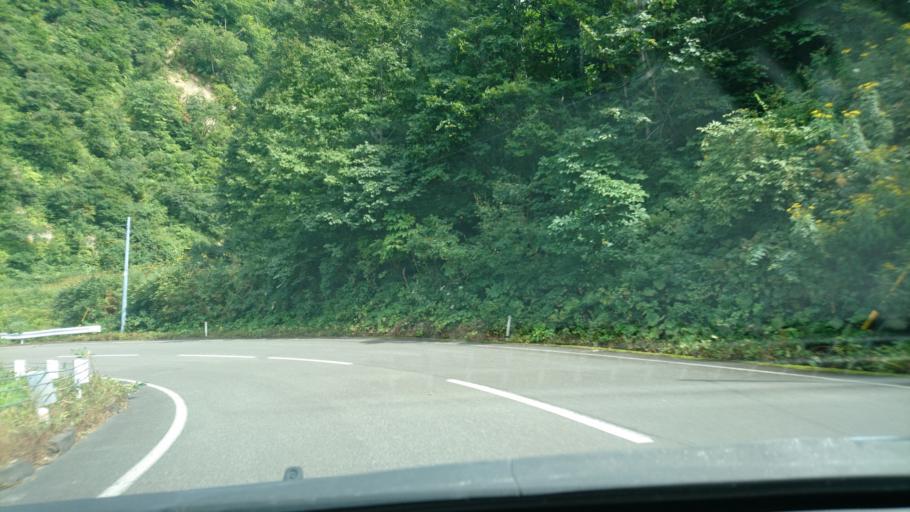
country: JP
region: Akita
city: Yuzawa
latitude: 39.0196
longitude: 140.7297
